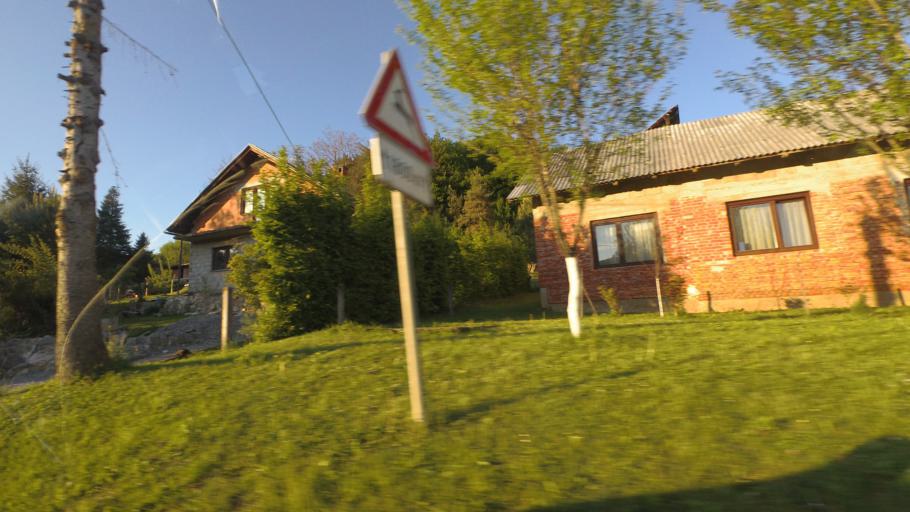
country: HR
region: Karlovacka
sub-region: Grad Karlovac
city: Karlovac
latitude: 45.4108
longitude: 15.5602
